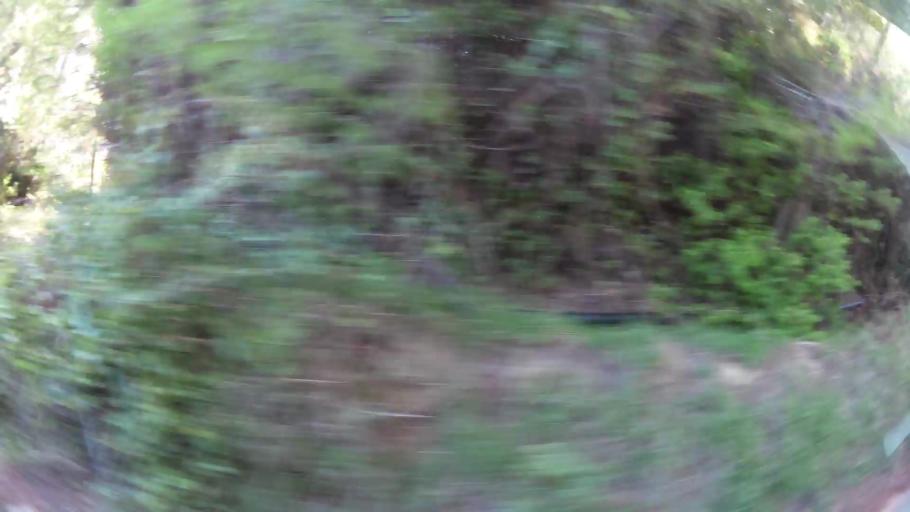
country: GR
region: Attica
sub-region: Nomarchia Anatolikis Attikis
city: Dioni
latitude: 38.0162
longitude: 23.9290
